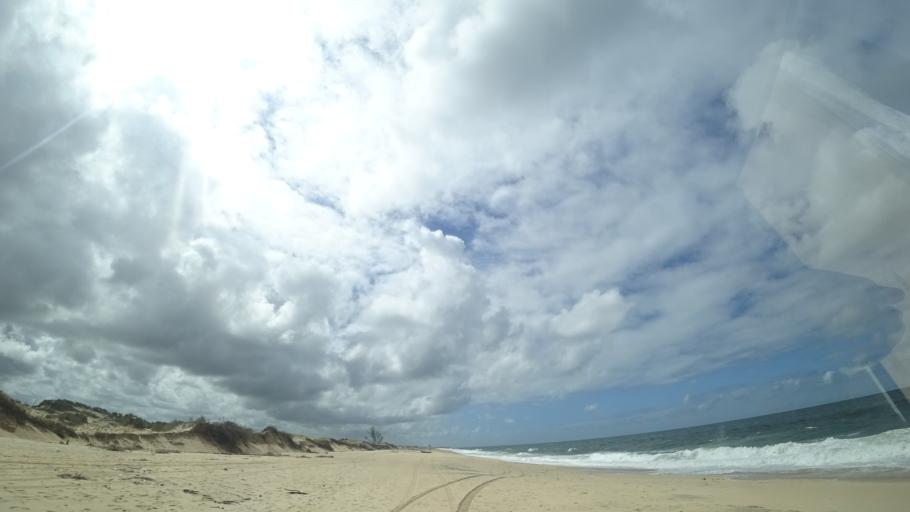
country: MZ
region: Sofala
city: Beira
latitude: -19.6189
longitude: 35.2163
